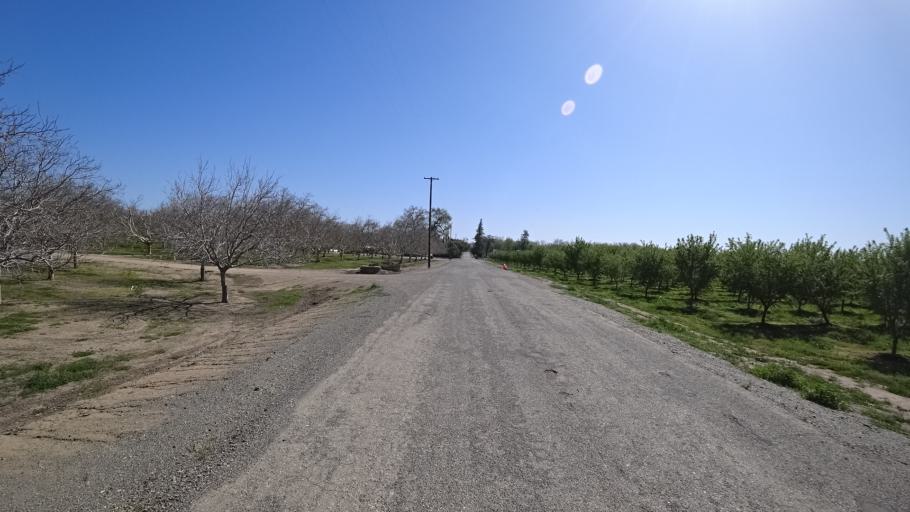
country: US
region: California
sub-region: Glenn County
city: Willows
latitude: 39.4501
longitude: -122.0225
